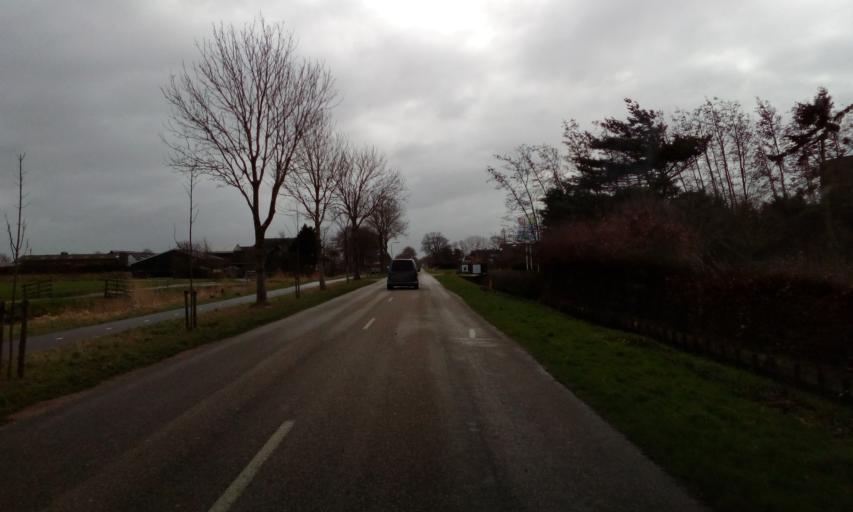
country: NL
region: North Holland
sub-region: Gemeente Uithoorn
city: Uithoorn
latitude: 52.2106
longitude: 4.8331
